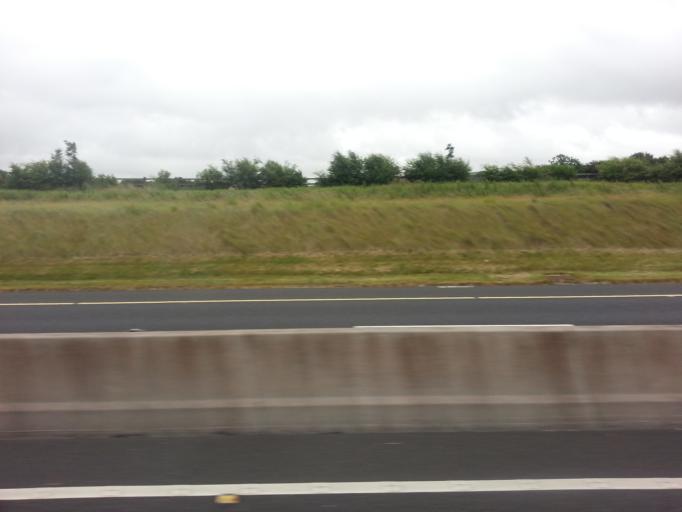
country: IE
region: Leinster
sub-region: Kildare
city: Castledermot
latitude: 52.9199
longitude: -6.8670
